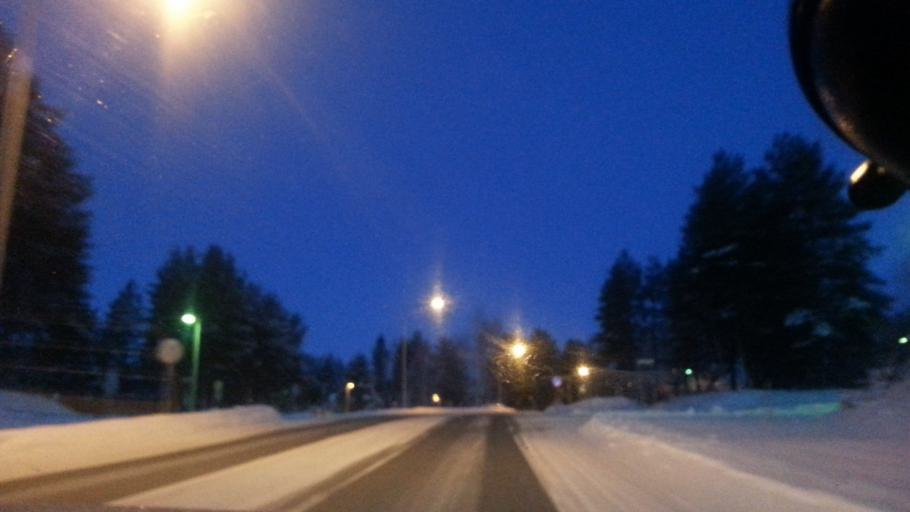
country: FI
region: Lapland
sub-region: Rovaniemi
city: Rovaniemi
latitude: 66.4937
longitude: 25.7571
